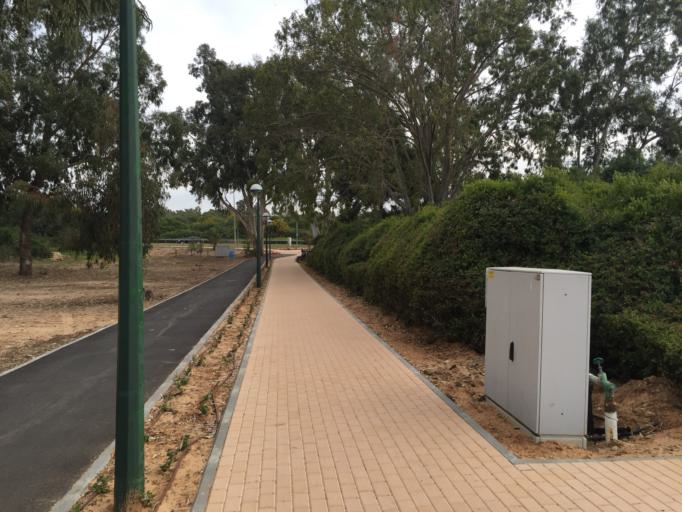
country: IL
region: Haifa
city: Qesarya
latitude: 32.5043
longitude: 34.9050
